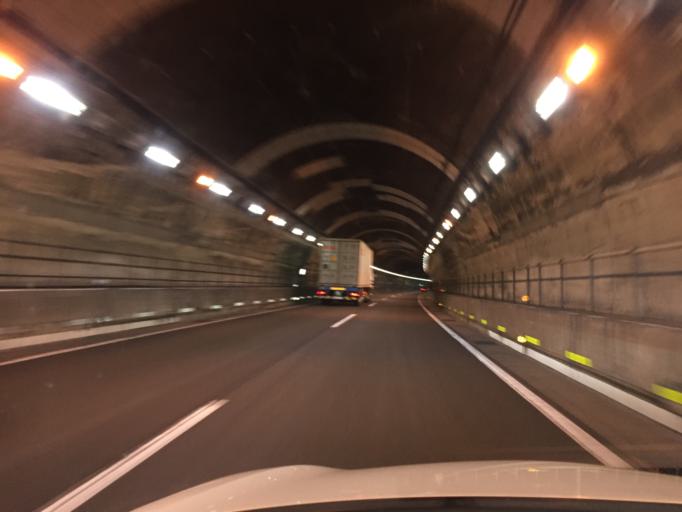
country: JP
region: Fukushima
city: Fukushima-shi
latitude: 37.6783
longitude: 140.4462
